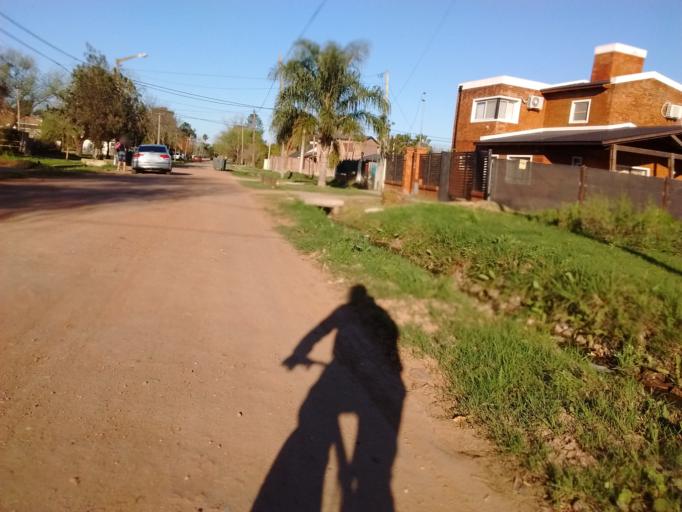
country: AR
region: Santa Fe
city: Funes
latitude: -32.9243
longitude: -60.7943
